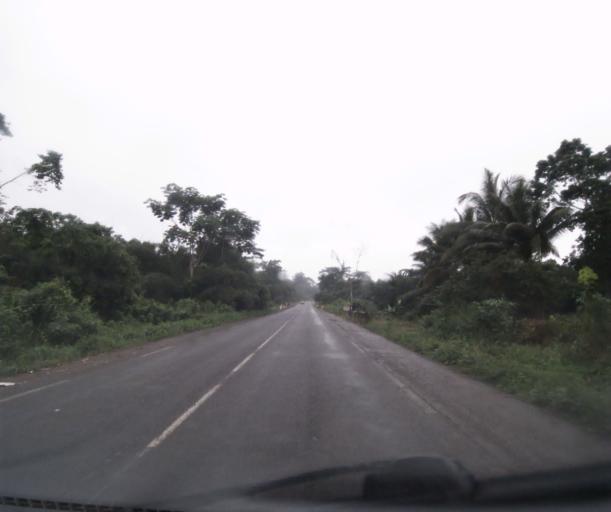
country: CM
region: Centre
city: Eseka
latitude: 3.8899
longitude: 10.7566
